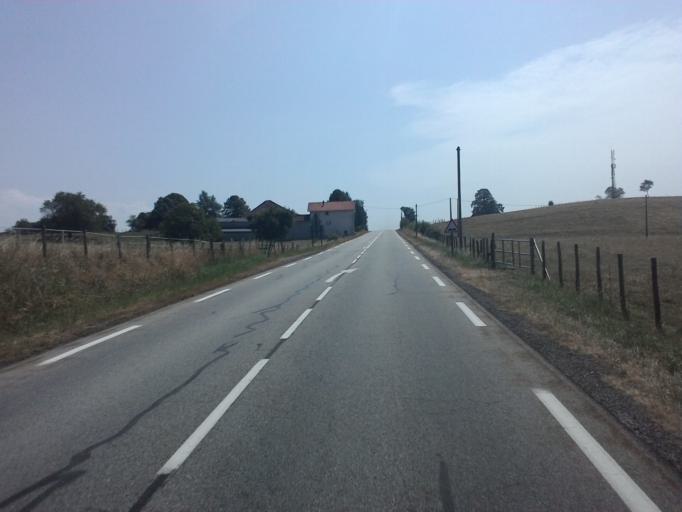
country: FR
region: Rhone-Alpes
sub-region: Departement de l'Isere
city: Montferrat
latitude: 45.4659
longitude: 5.5799
